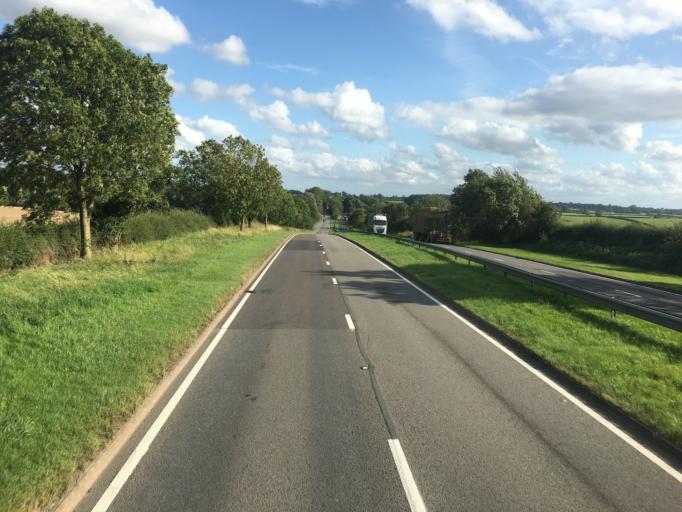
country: GB
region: England
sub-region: Leicestershire
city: Lutterworth
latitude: 52.4395
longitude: -1.2413
